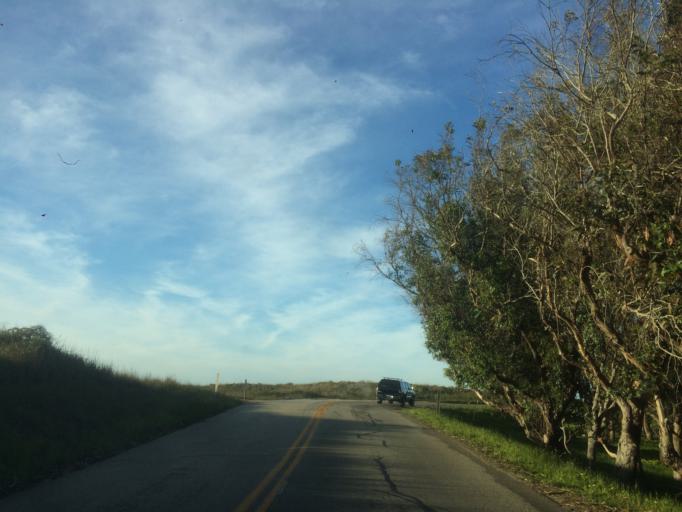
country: US
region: California
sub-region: San Luis Obispo County
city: Los Osos
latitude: 35.2967
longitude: -120.8689
